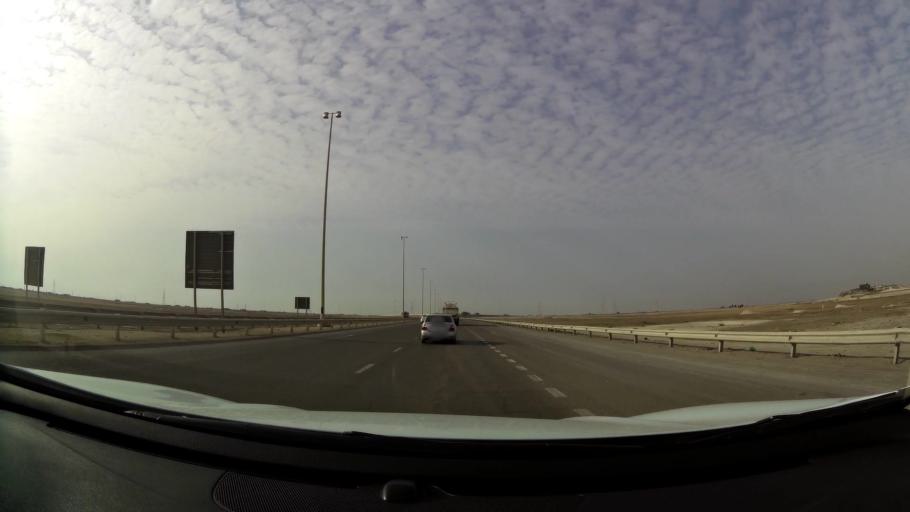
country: AE
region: Abu Dhabi
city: Abu Dhabi
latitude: 24.2053
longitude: 54.4192
